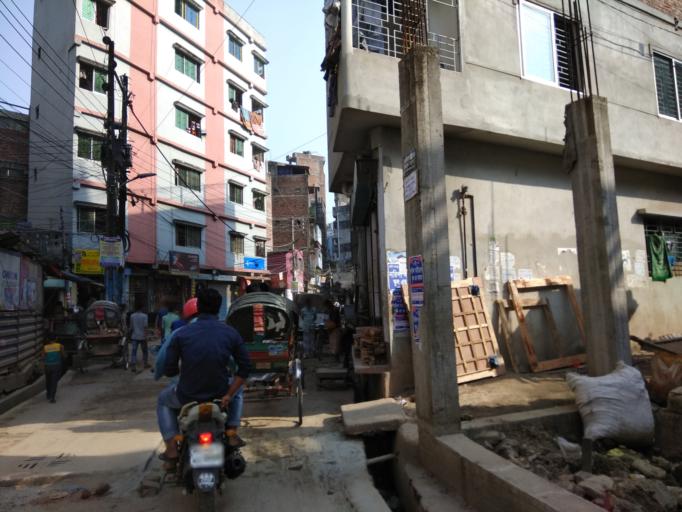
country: BD
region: Dhaka
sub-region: Dhaka
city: Dhaka
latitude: 23.7223
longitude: 90.4033
